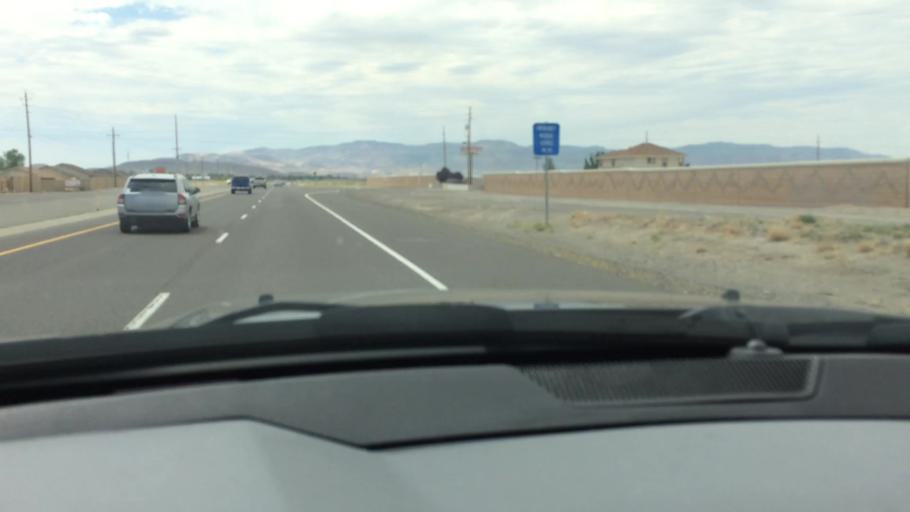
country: US
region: Nevada
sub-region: Lyon County
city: Fernley
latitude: 39.5995
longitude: -119.2049
